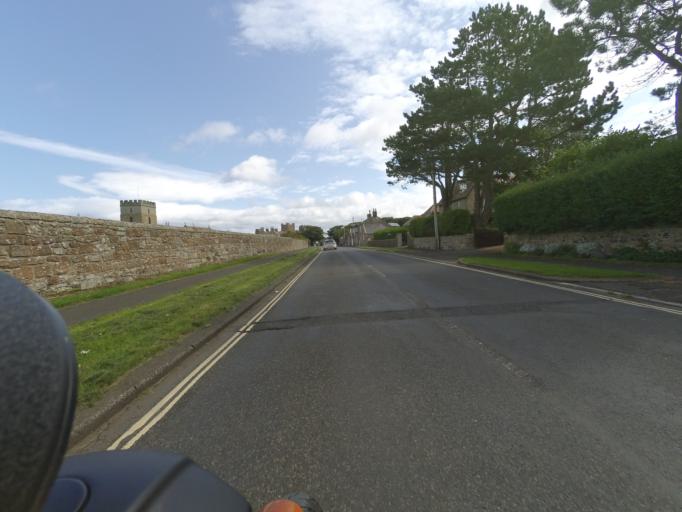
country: GB
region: England
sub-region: Northumberland
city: Bamburgh
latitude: 55.6072
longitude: -1.7199
